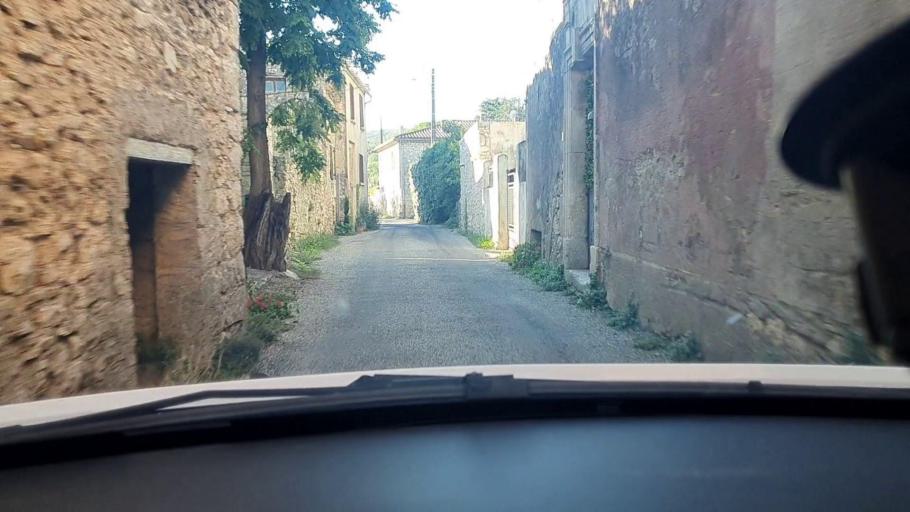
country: FR
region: Languedoc-Roussillon
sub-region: Departement du Gard
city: Goudargues
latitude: 44.2351
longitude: 4.4423
